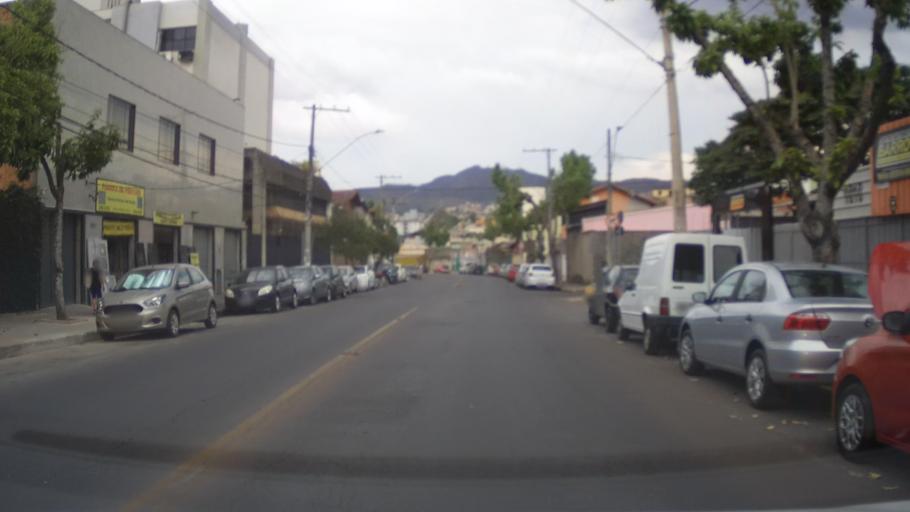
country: BR
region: Minas Gerais
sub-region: Belo Horizonte
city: Belo Horizonte
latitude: -19.9064
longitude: -43.9152
